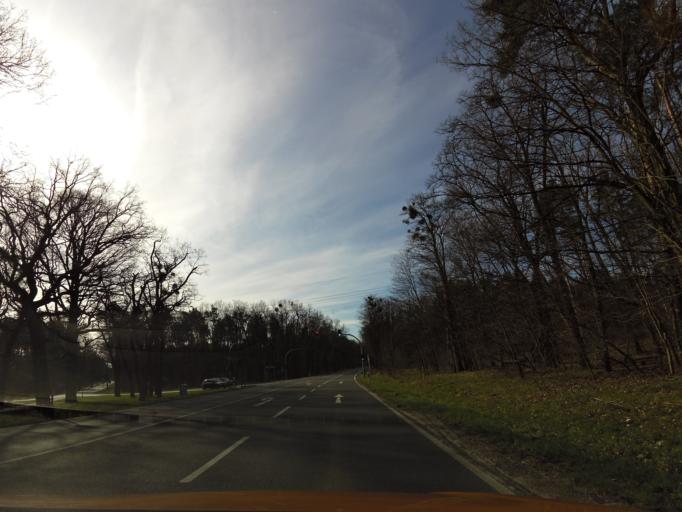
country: DE
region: Brandenburg
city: Michendorf
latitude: 52.3455
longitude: 13.0455
